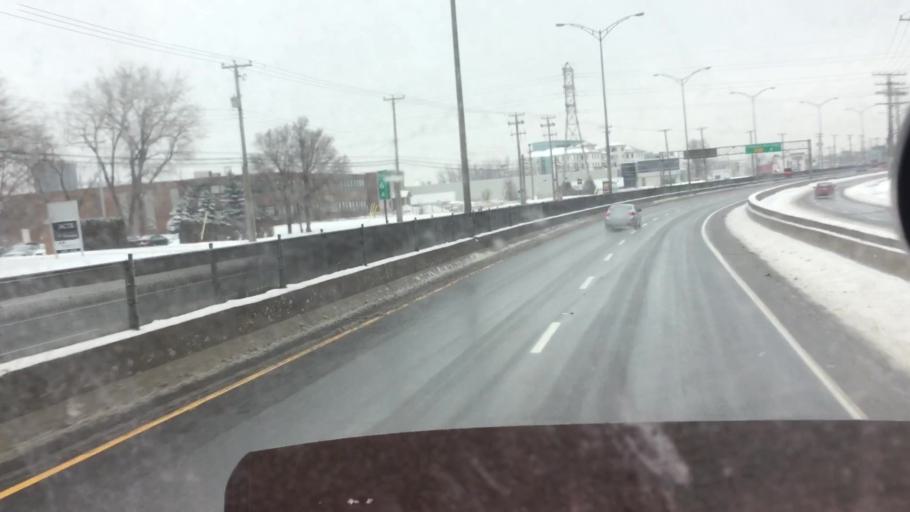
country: CA
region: Quebec
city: Saint-Laurent
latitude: 45.4887
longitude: -73.6877
